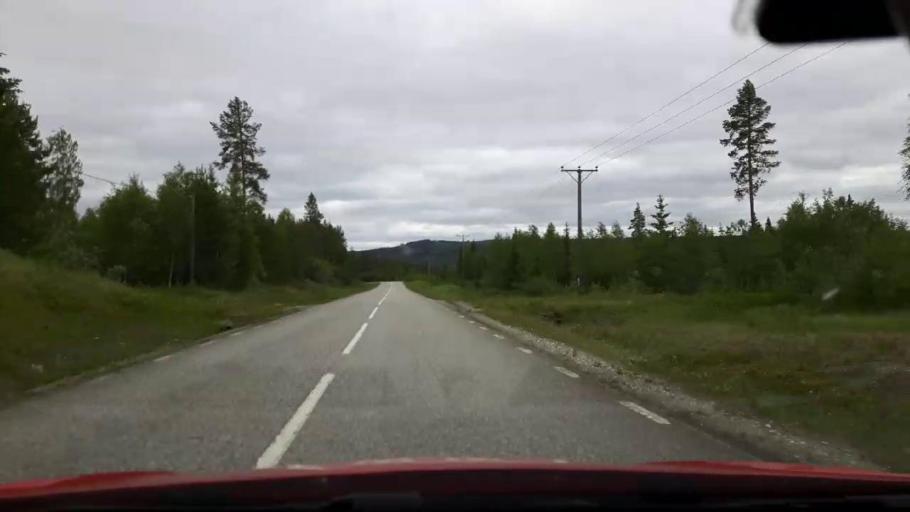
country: SE
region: Jaemtland
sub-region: Stroemsunds Kommun
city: Stroemsund
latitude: 63.3024
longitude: 15.7597
